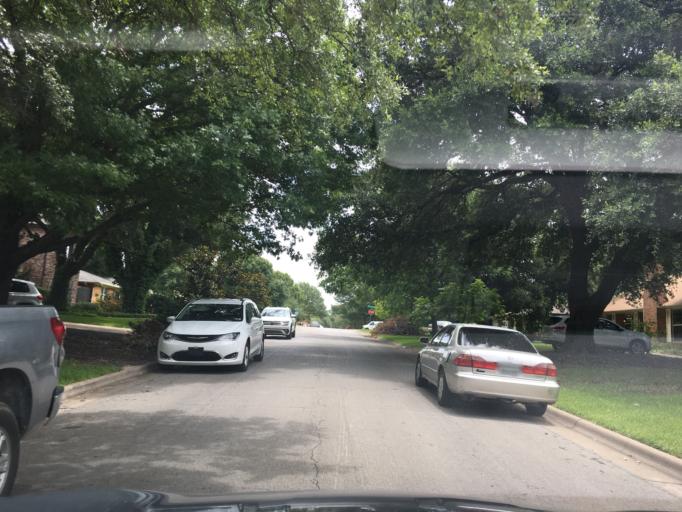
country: US
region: Texas
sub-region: Dallas County
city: University Park
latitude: 32.8974
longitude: -96.7891
